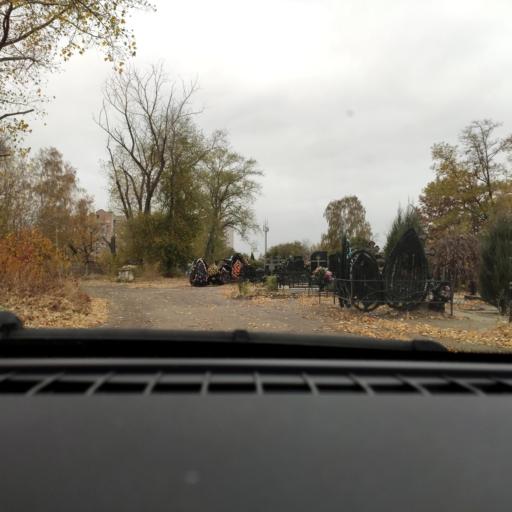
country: RU
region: Voronezj
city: Voronezh
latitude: 51.6614
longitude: 39.2918
